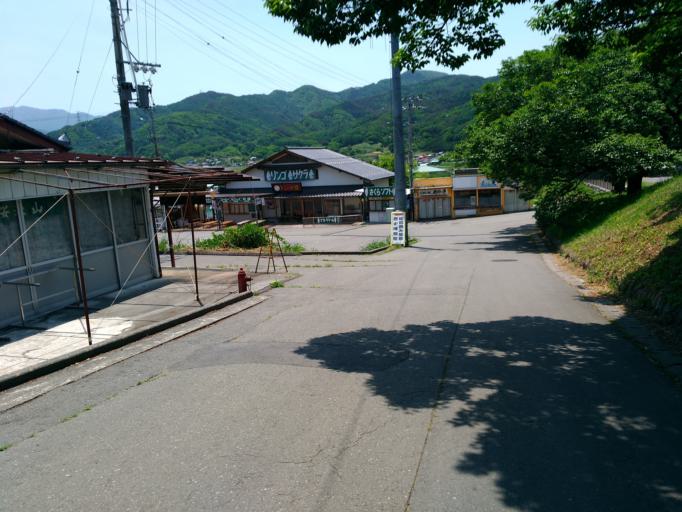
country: JP
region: Nagano
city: Ina
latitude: 35.8319
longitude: 138.0636
